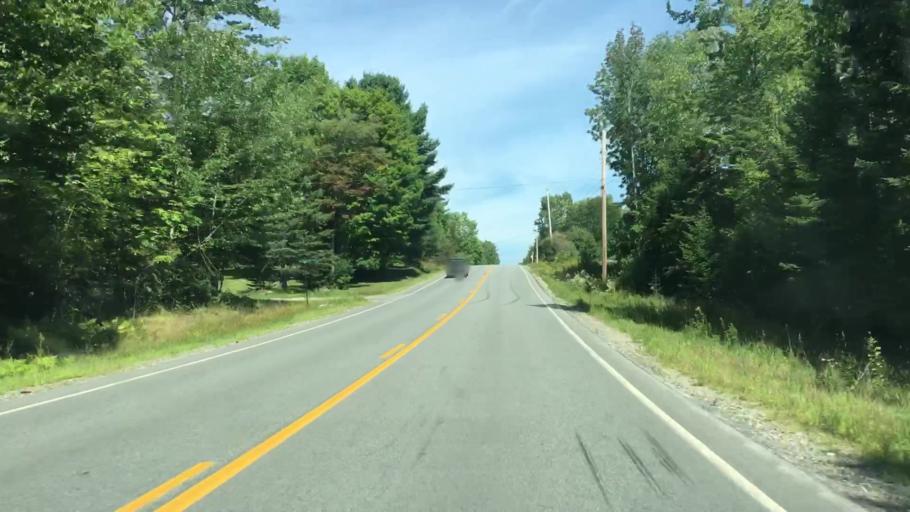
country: US
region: Maine
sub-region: Penobscot County
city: Howland
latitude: 45.2109
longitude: -68.8003
